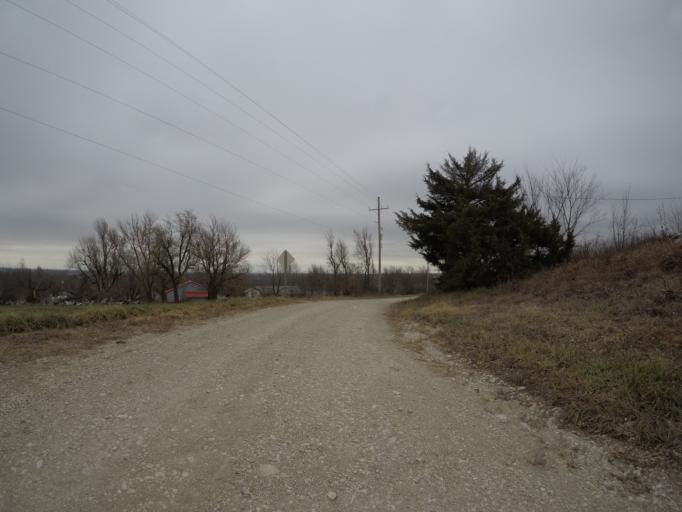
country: US
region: Kansas
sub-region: Wabaunsee County
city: Alma
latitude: 38.8608
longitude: -96.1134
